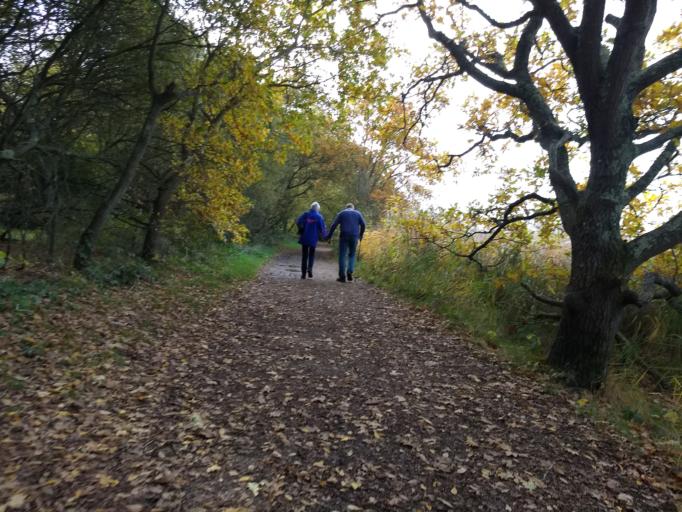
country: GB
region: England
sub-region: Isle of Wight
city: Freshwater
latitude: 50.6933
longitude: -1.5001
